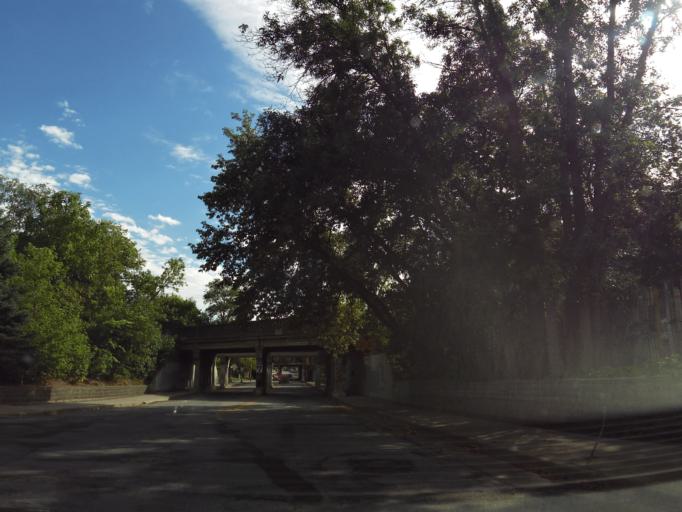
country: US
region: Minnesota
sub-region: Hennepin County
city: Minneapolis
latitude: 45.0071
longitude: -93.2526
